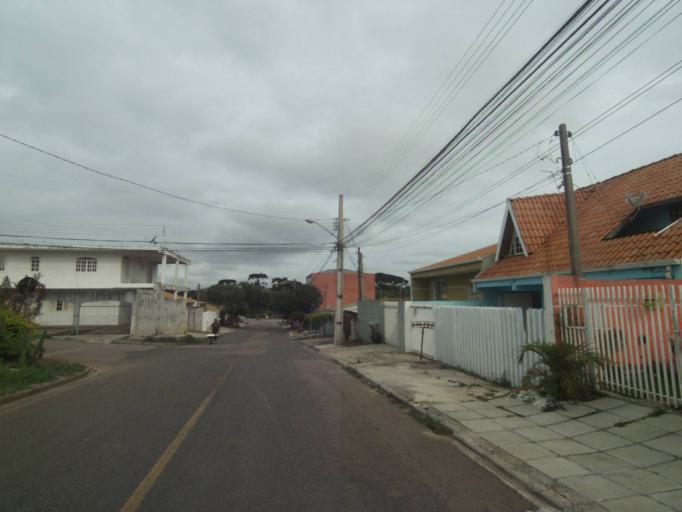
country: BR
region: Parana
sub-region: Sao Jose Dos Pinhais
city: Sao Jose dos Pinhais
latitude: -25.5534
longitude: -49.2699
